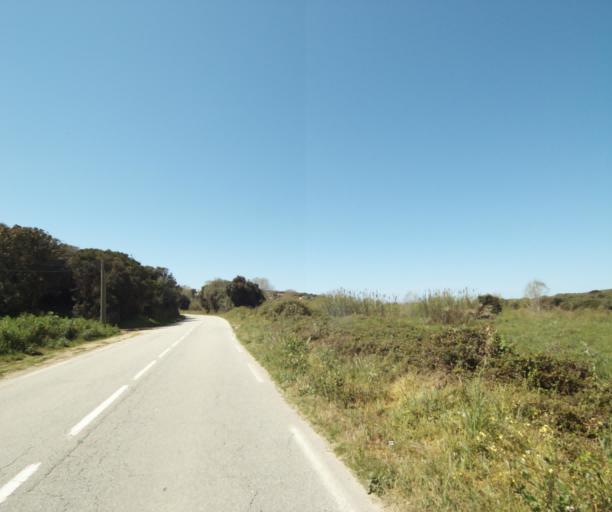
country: FR
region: Corsica
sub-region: Departement de la Corse-du-Sud
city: Propriano
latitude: 41.6587
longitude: 8.9093
